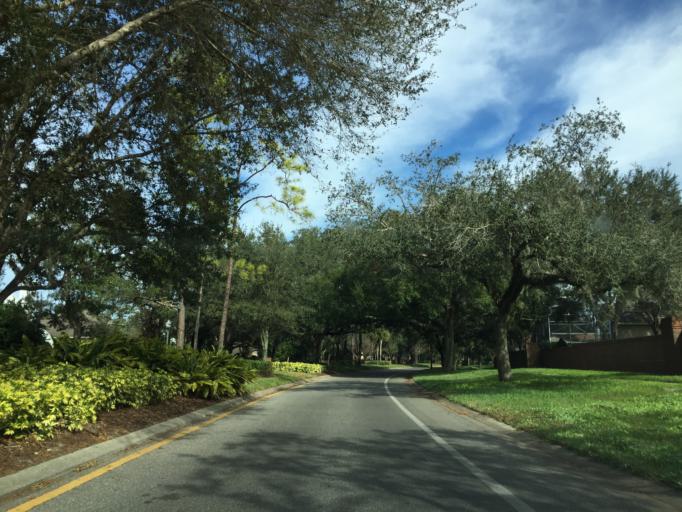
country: US
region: Florida
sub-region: Seminole County
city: Oviedo
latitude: 28.6767
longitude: -81.2585
